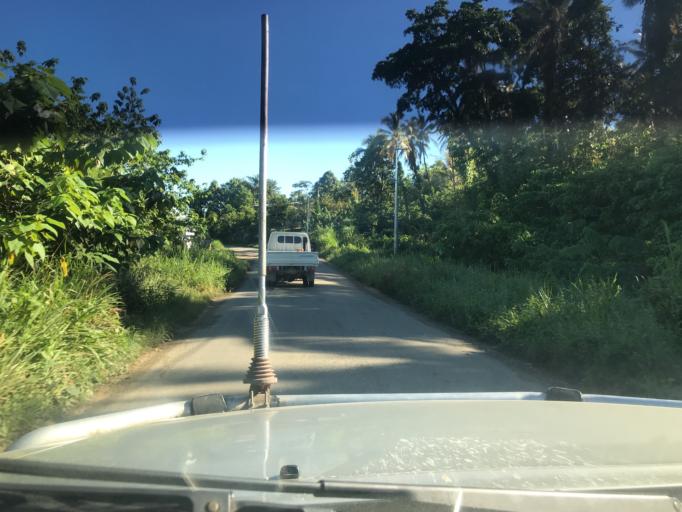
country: SB
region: Malaita
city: Auki
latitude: -8.7602
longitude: 160.6957
